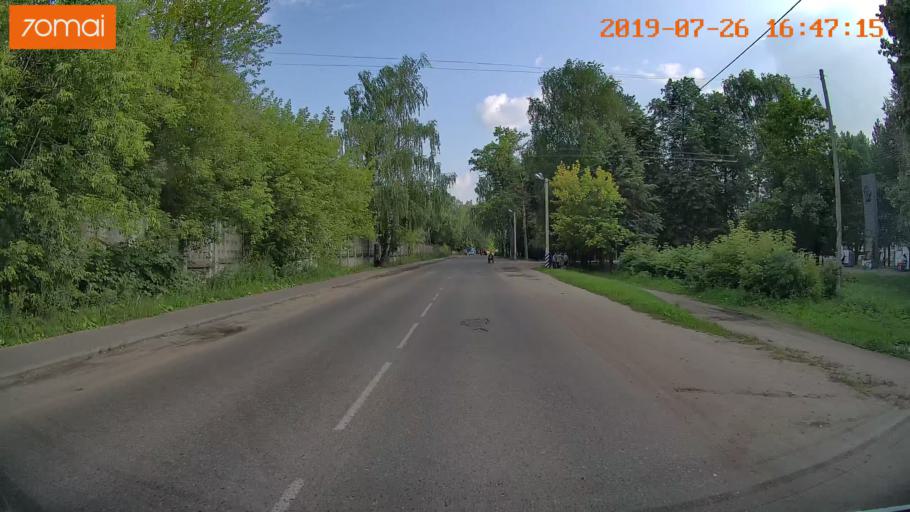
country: RU
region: Ivanovo
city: Bogorodskoye
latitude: 57.0429
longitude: 41.0116
